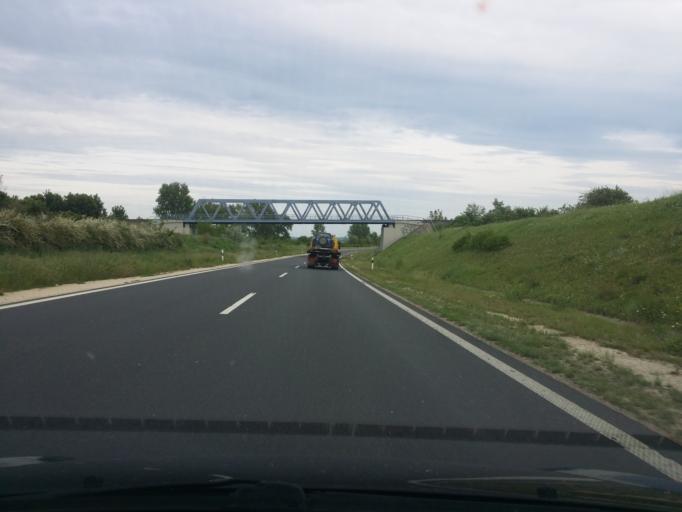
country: HU
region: Fejer
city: Lepseny
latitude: 47.0251
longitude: 18.1792
